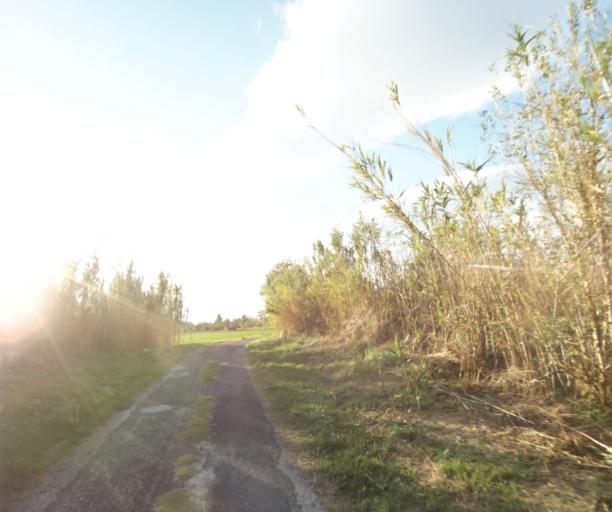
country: FR
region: Languedoc-Roussillon
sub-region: Departement des Pyrenees-Orientales
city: Latour-Bas-Elne
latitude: 42.5806
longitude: 3.0041
